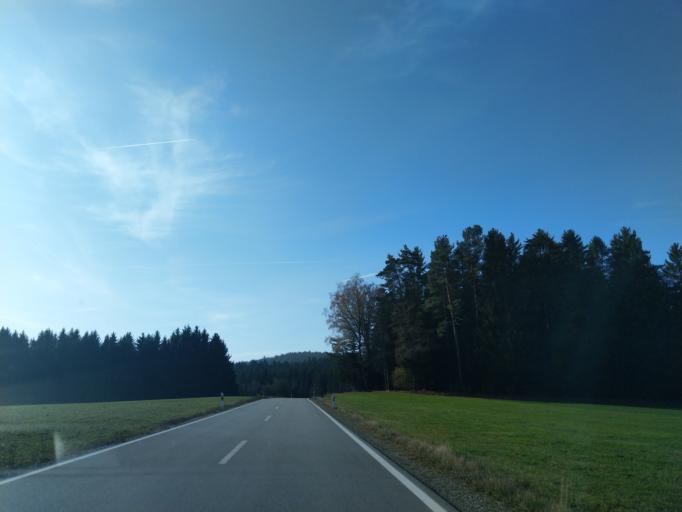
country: DE
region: Bavaria
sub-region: Lower Bavaria
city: Lalling
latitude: 48.8882
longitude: 13.1305
